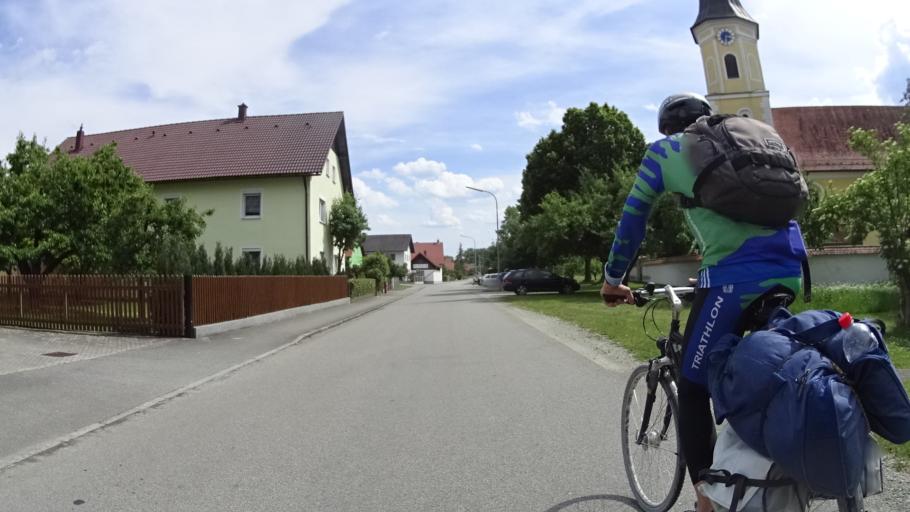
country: DE
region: Bavaria
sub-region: Upper Palatinate
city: Wiesent
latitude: 48.9941
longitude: 12.3485
